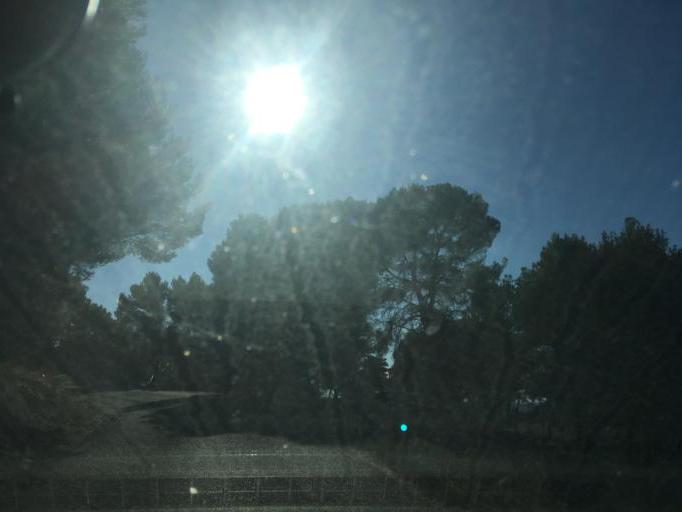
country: FR
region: Provence-Alpes-Cote d'Azur
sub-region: Departement du Var
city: Regusse
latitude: 43.7093
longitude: 6.1436
